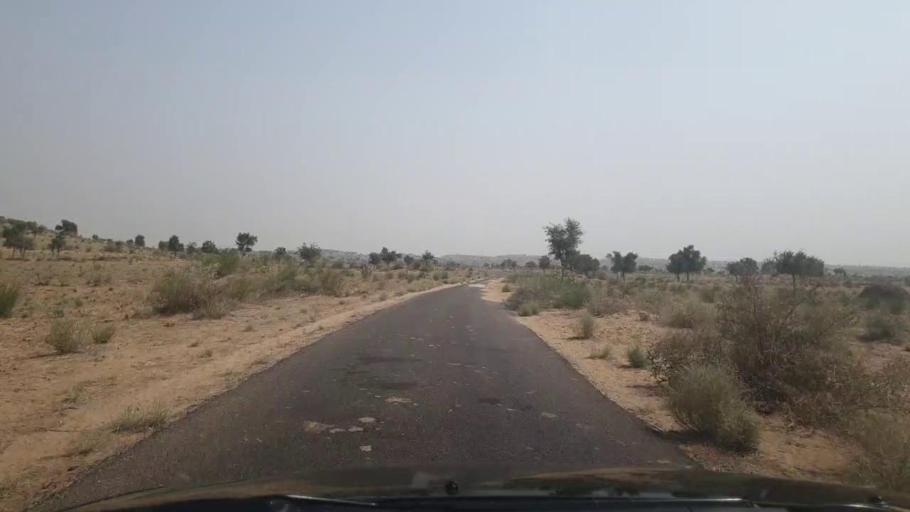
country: PK
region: Sindh
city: Islamkot
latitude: 24.9451
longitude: 70.3917
